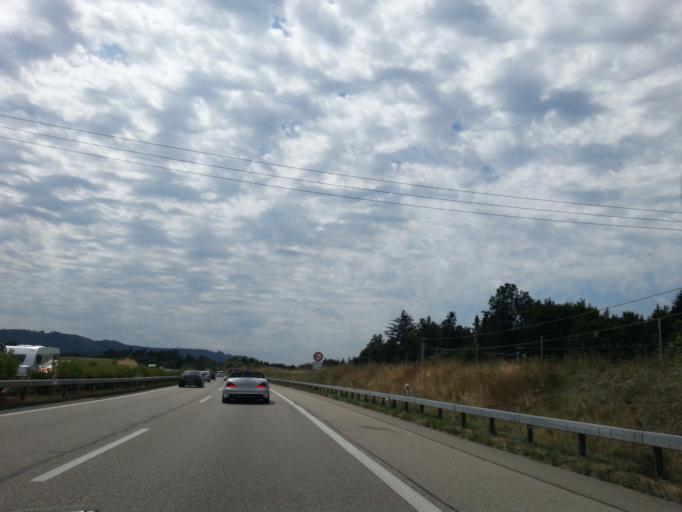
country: CH
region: Bern
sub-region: Emmental District
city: Hindelbank
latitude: 47.0464
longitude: 7.5309
